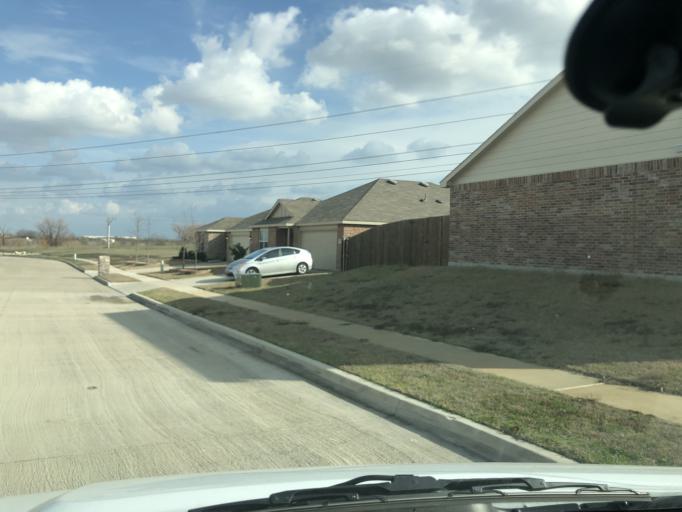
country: US
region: Texas
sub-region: Tarrant County
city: Saginaw
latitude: 32.9108
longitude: -97.3670
